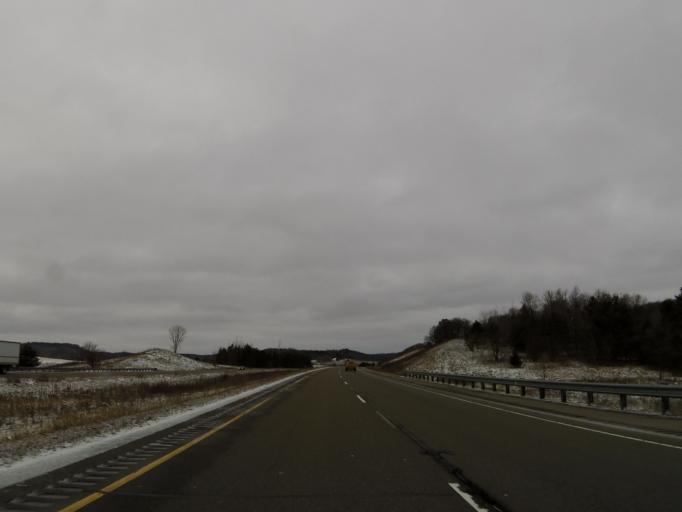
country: US
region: Wisconsin
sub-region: Jackson County
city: Black River Falls
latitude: 44.4129
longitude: -91.0434
